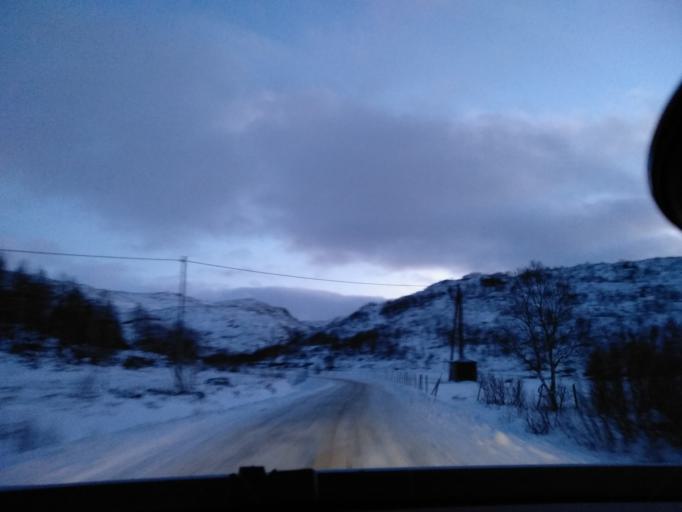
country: NO
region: Vest-Agder
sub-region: Sirdal
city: Tonstad
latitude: 59.0215
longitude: 6.9274
